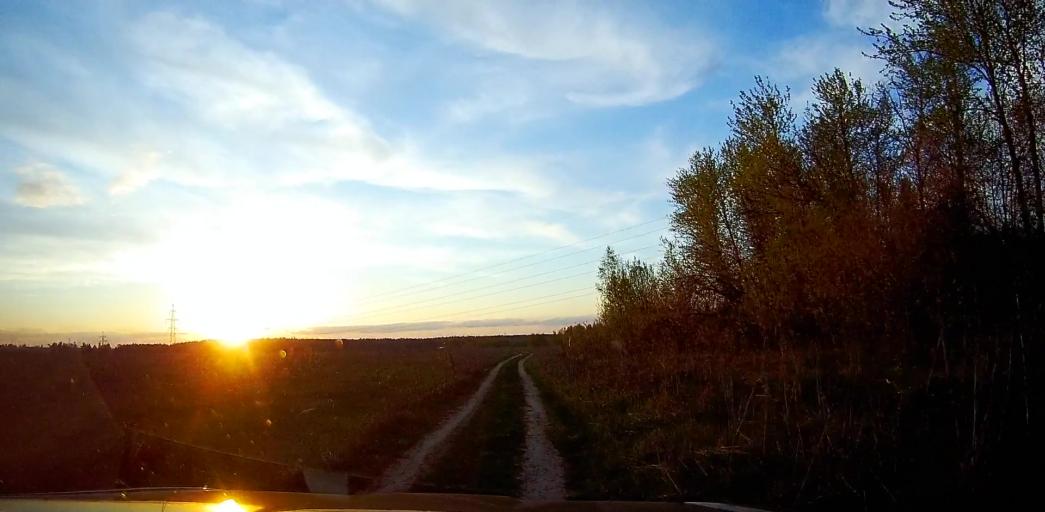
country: RU
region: Moskovskaya
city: Peski
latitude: 55.2329
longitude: 38.7301
